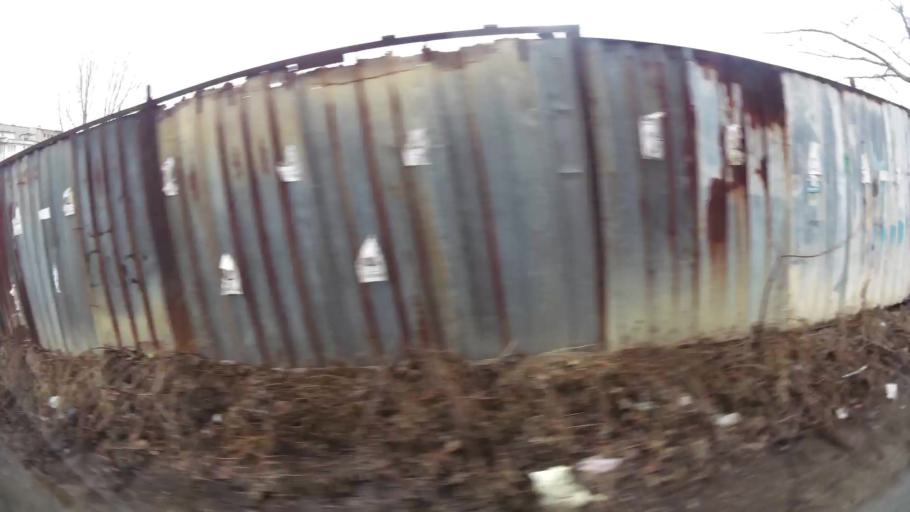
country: BG
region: Sofiya
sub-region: Obshtina Bozhurishte
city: Bozhurishte
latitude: 42.7257
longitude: 23.2592
